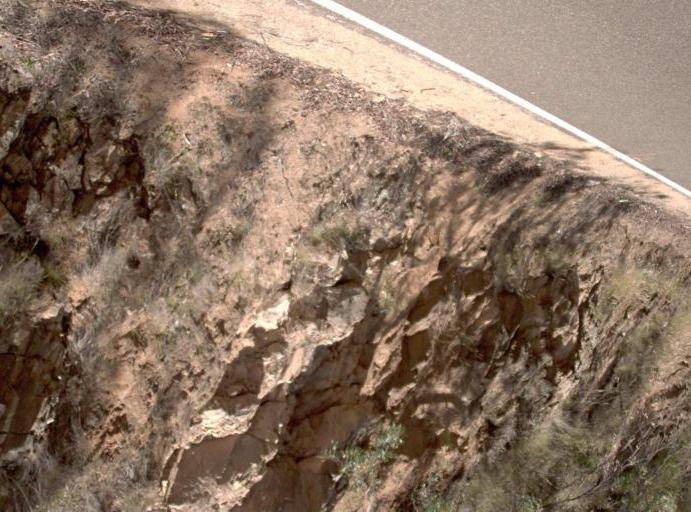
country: AU
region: Victoria
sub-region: East Gippsland
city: Bairnsdale
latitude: -37.4864
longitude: 147.8328
